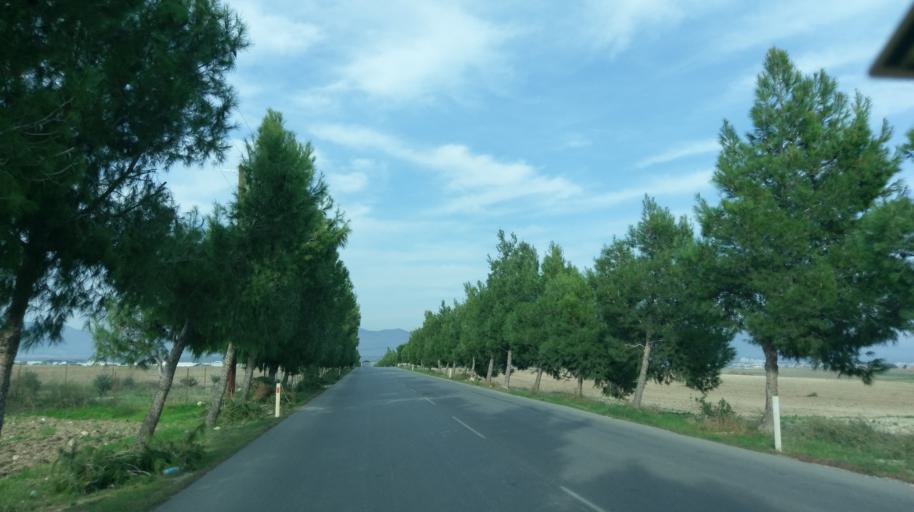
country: CY
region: Lefkosia
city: Mammari
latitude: 35.1919
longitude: 33.2641
